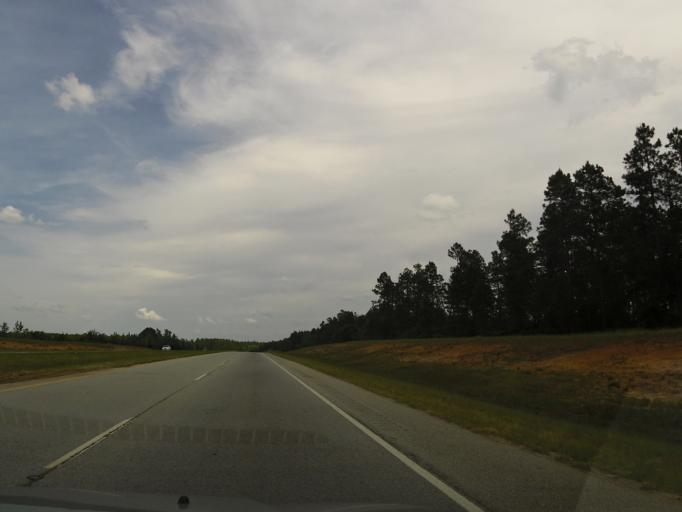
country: US
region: Georgia
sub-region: Emanuel County
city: Swainsboro
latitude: 32.6354
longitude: -82.3726
